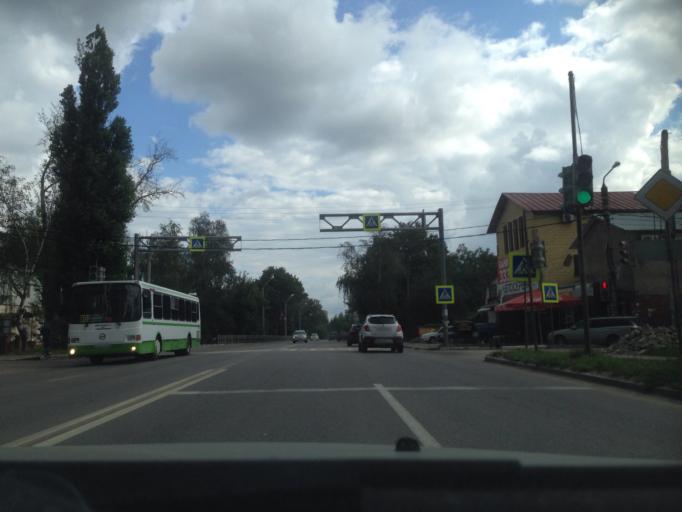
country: RU
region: Voronezj
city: Podgornoye
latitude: 51.7268
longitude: 39.1942
